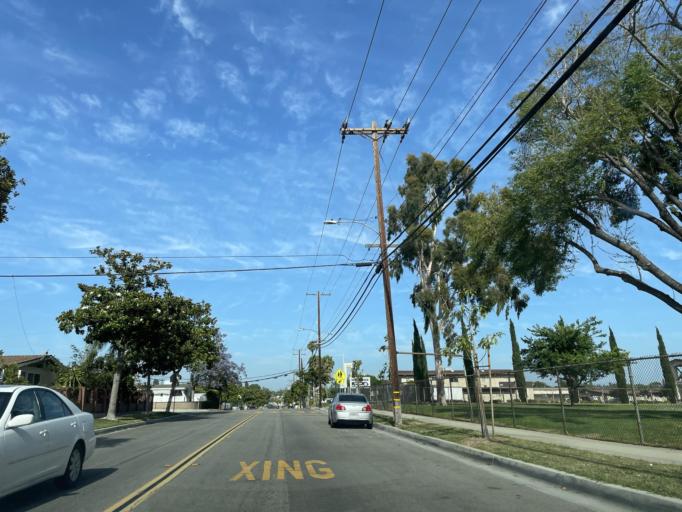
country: US
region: California
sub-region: Los Angeles County
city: La Mirada
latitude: 33.9098
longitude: -118.0339
